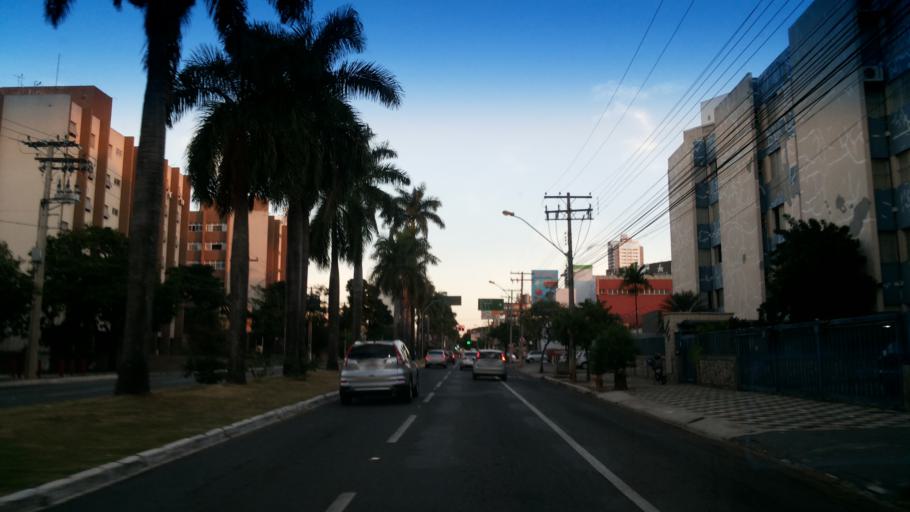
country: BR
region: Goias
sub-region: Goiania
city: Goiania
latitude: -16.6995
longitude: -49.2644
